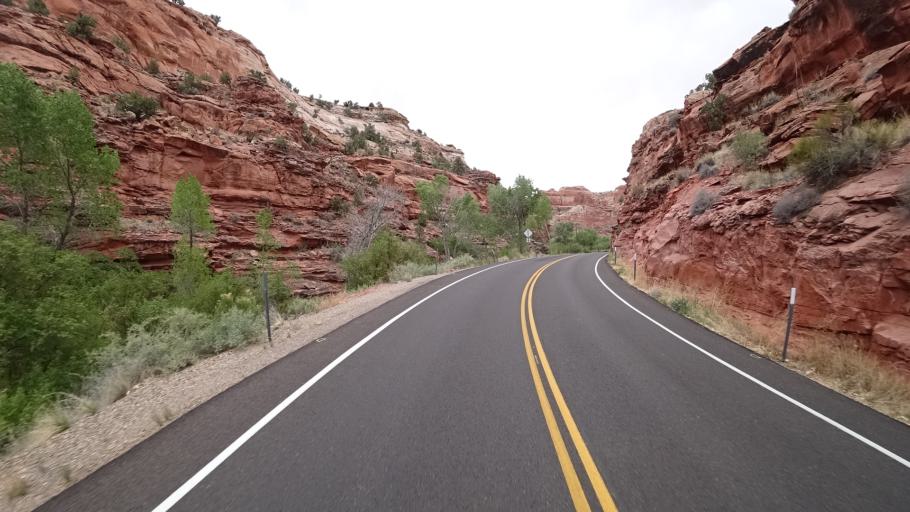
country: US
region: Utah
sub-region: Wayne County
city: Loa
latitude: 37.7792
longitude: -111.4186
